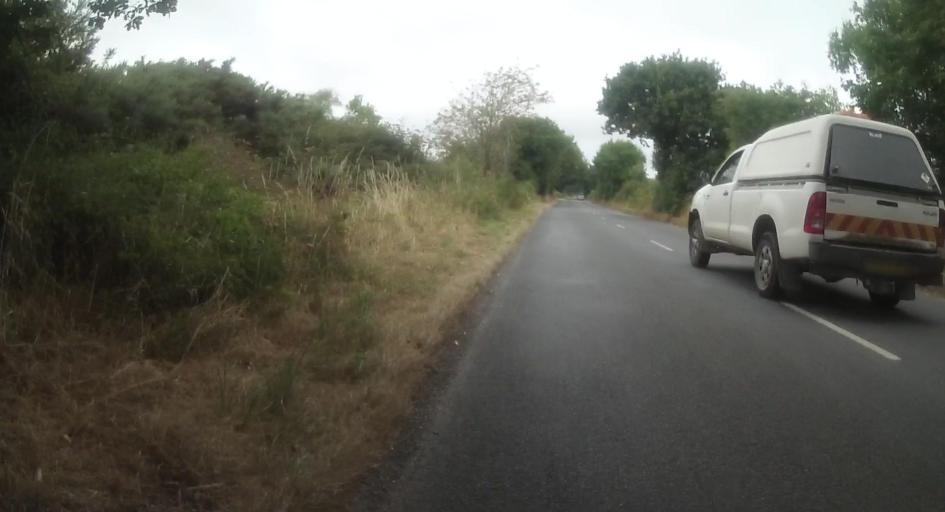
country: GB
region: England
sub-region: Dorset
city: Wareham
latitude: 50.6863
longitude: -2.1528
